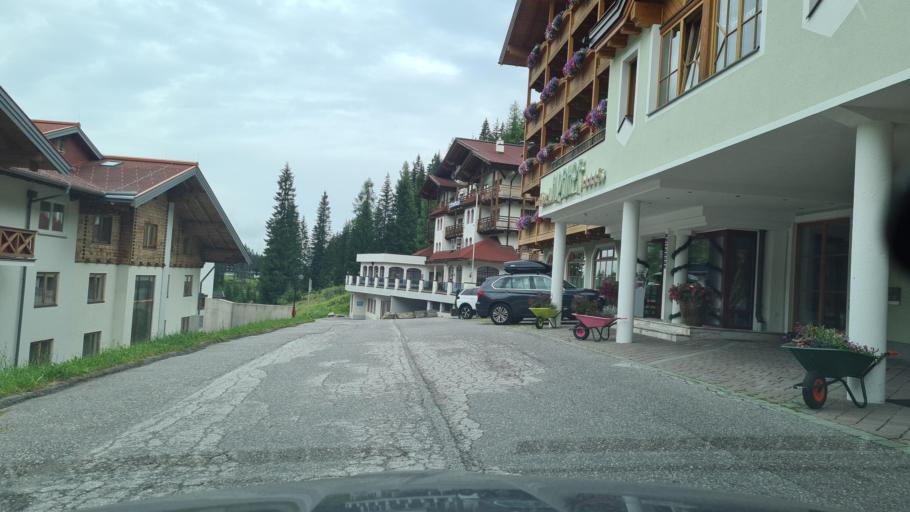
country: AT
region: Salzburg
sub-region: Politischer Bezirk Sankt Johann im Pongau
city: Untertauern
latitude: 47.2933
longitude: 13.4580
